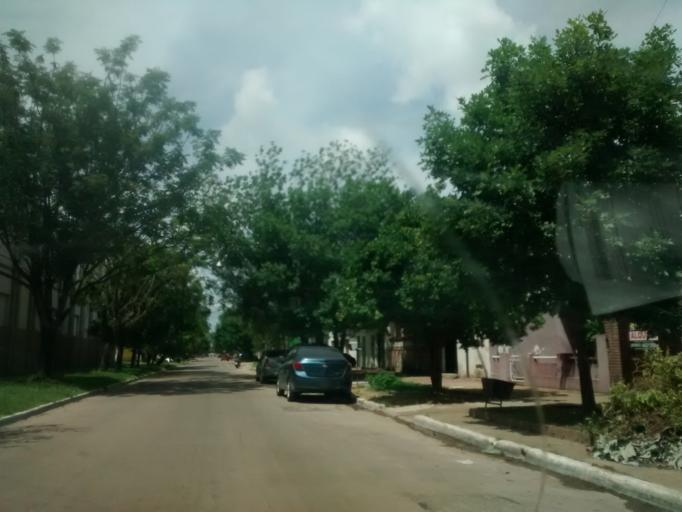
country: AR
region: Chaco
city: Resistencia
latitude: -27.4451
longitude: -58.9903
